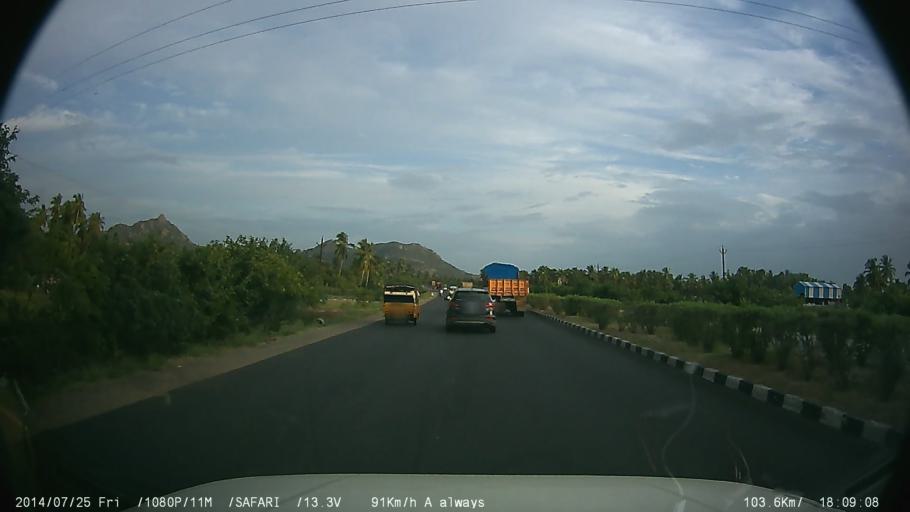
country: IN
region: Tamil Nadu
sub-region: Krishnagiri
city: Kaverippattanam
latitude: 12.3927
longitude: 78.2189
